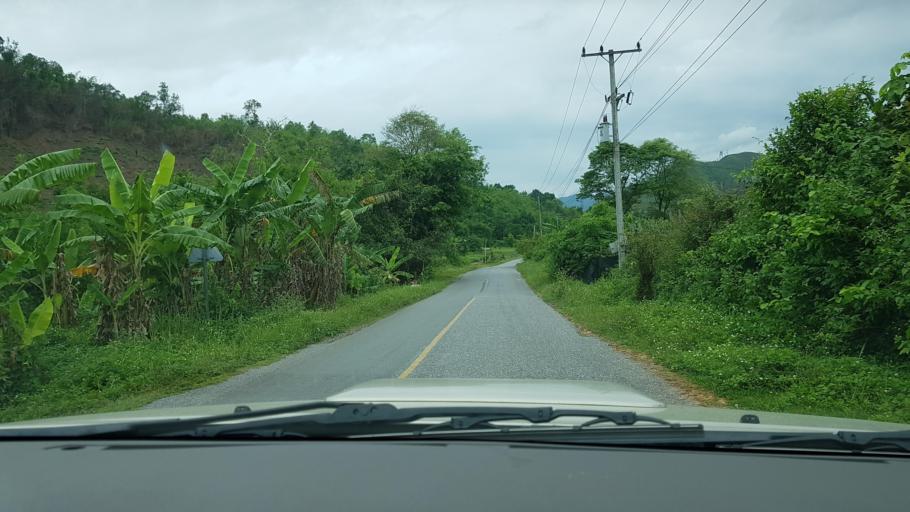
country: LA
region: Loungnamtha
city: Muang Nale
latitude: 20.3752
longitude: 101.7321
